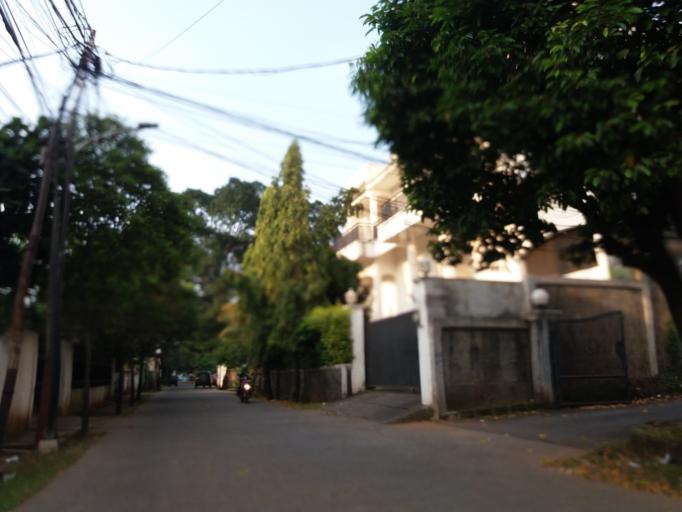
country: ID
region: Jakarta Raya
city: Jakarta
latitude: -6.2419
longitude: 106.8151
